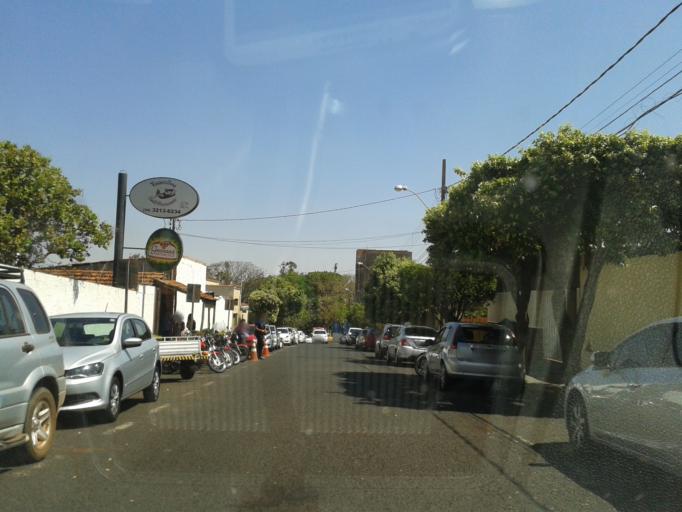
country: BR
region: Minas Gerais
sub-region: Uberlandia
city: Uberlandia
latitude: -18.9069
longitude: -48.2425
